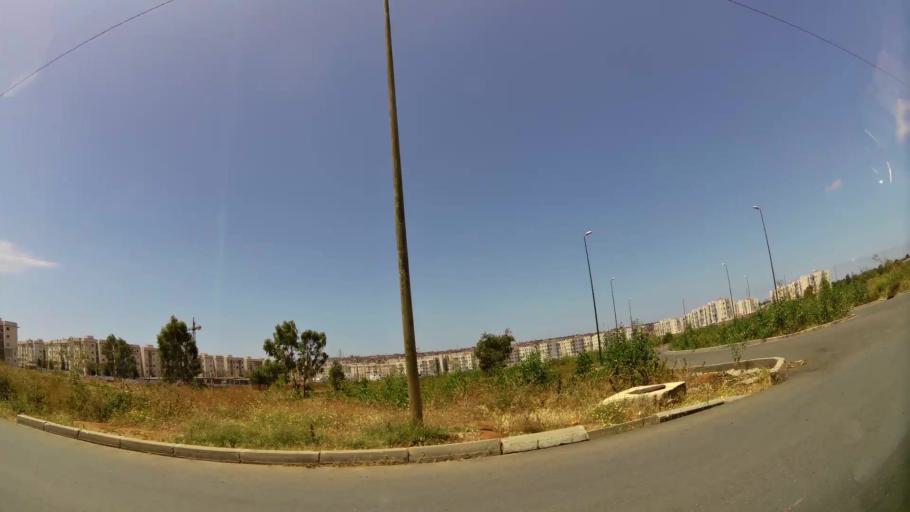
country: MA
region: Gharb-Chrarda-Beni Hssen
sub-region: Kenitra Province
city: Kenitra
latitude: 34.2513
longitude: -6.6338
